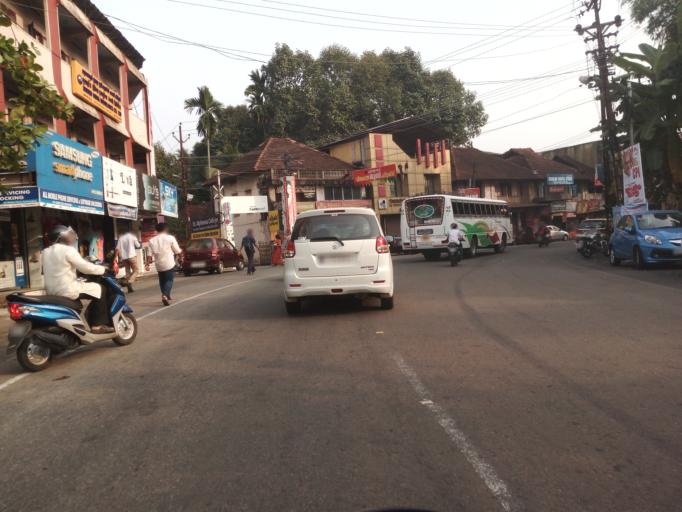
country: IN
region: Kerala
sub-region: Ernakulam
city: Muvattupula
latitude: 9.8996
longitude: 76.7140
